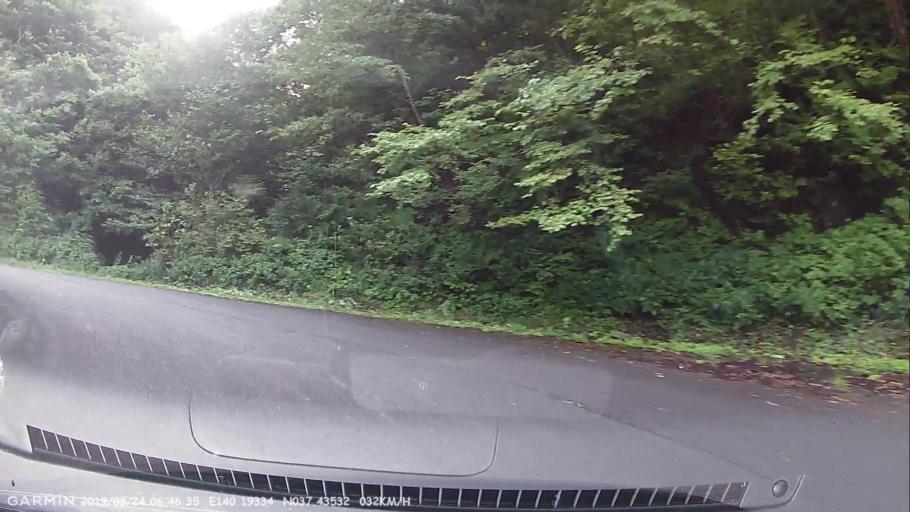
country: JP
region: Fukushima
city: Inawashiro
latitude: 37.4353
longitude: 140.1934
